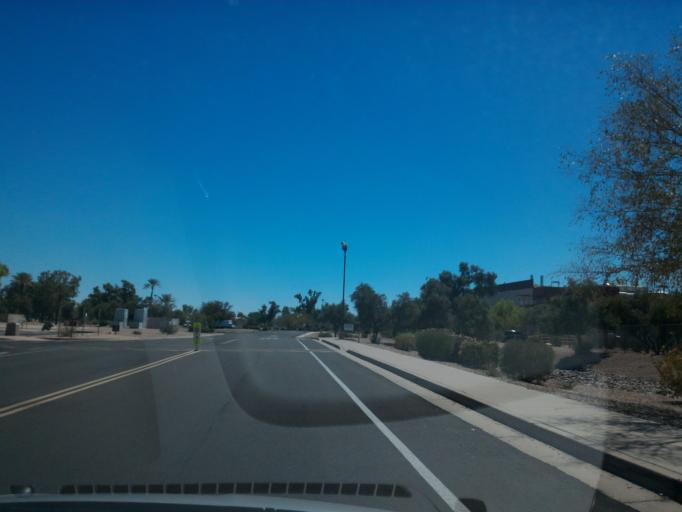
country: US
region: Arizona
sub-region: Maricopa County
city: Guadalupe
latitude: 33.3089
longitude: -111.9296
